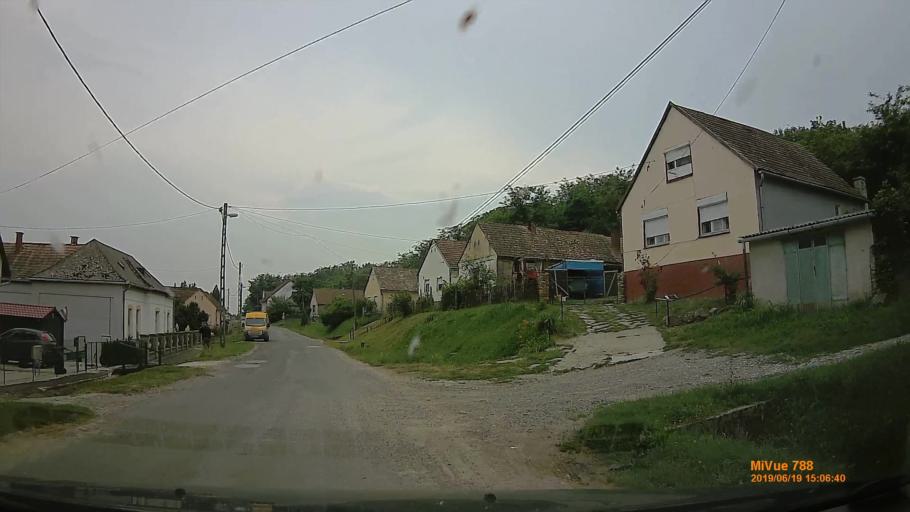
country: HU
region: Baranya
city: Szigetvar
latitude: 46.0965
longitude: 17.8065
